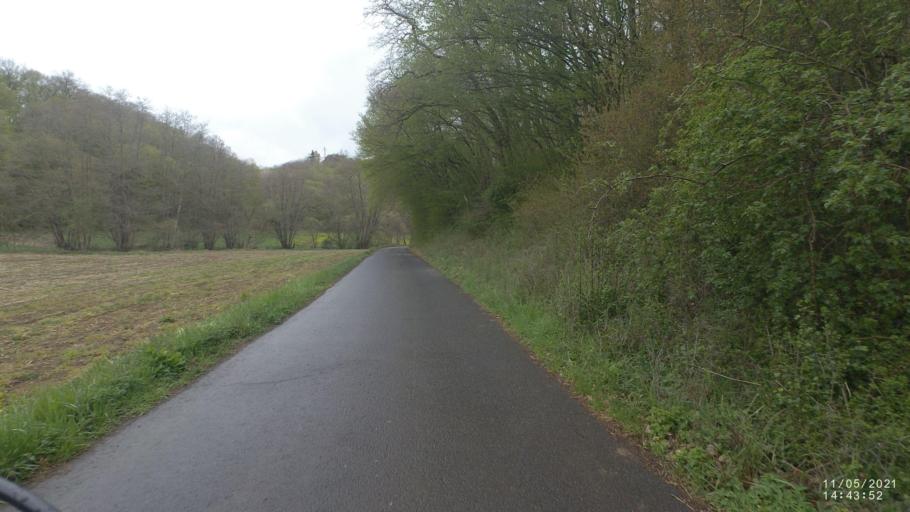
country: DE
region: Rheinland-Pfalz
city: Bermel
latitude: 50.2886
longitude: 7.0848
